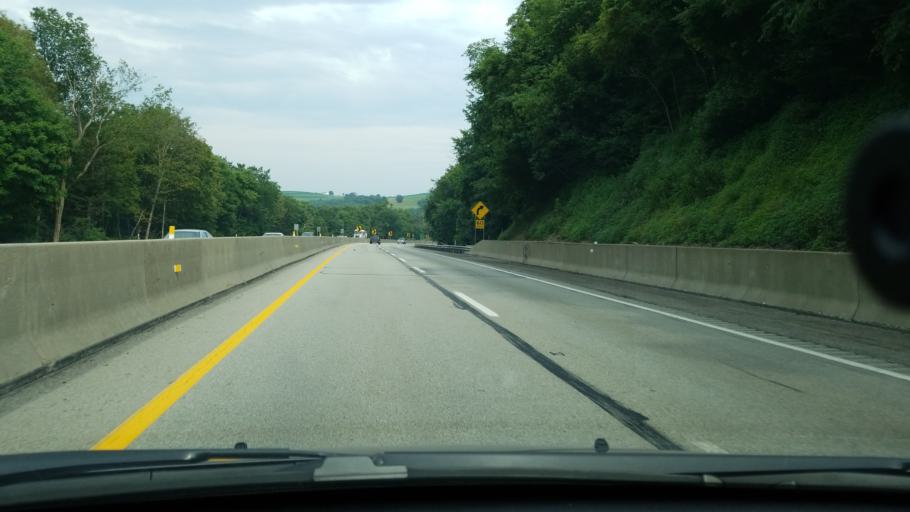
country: US
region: Pennsylvania
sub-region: Lawrence County
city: Ellport
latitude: 40.7855
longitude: -80.2453
